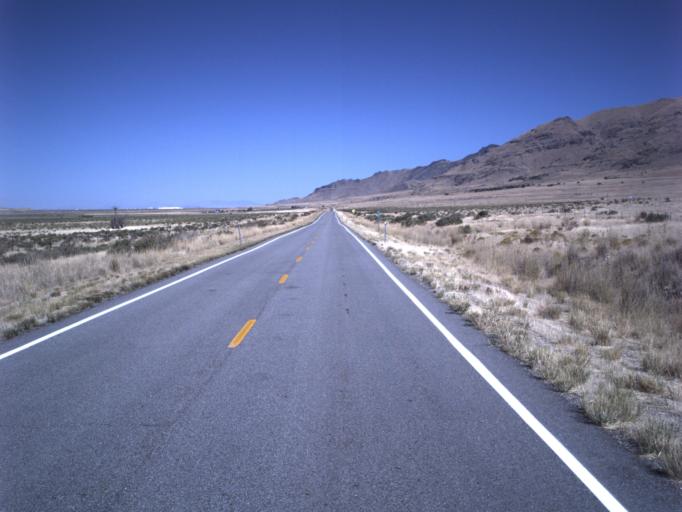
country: US
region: Utah
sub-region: Tooele County
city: Grantsville
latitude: 40.6488
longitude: -112.6854
